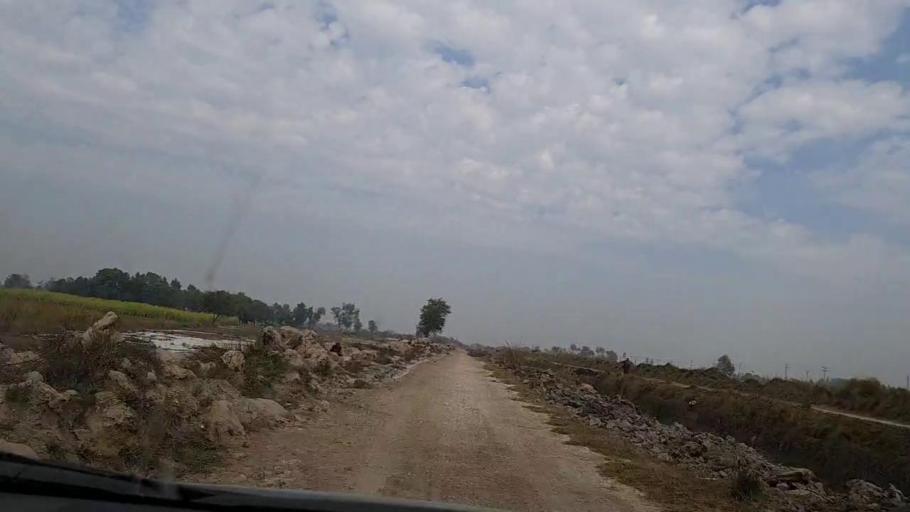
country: PK
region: Sindh
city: Daulatpur
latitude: 26.5632
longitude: 67.9836
